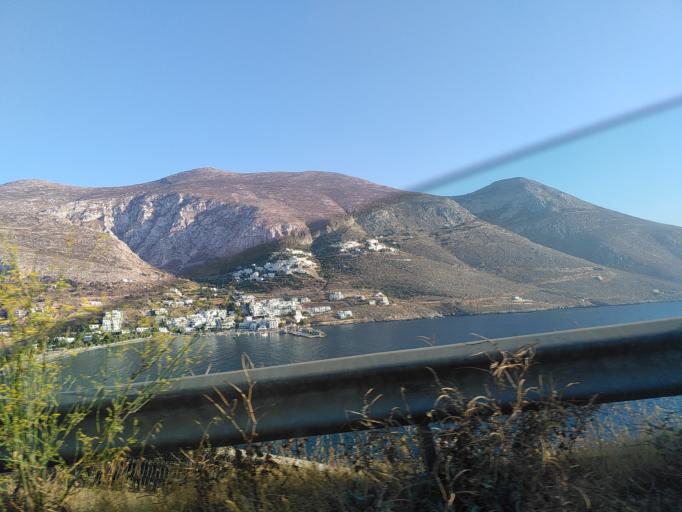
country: GR
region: South Aegean
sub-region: Nomos Kykladon
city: Amorgos
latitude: 36.9081
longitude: 25.9742
